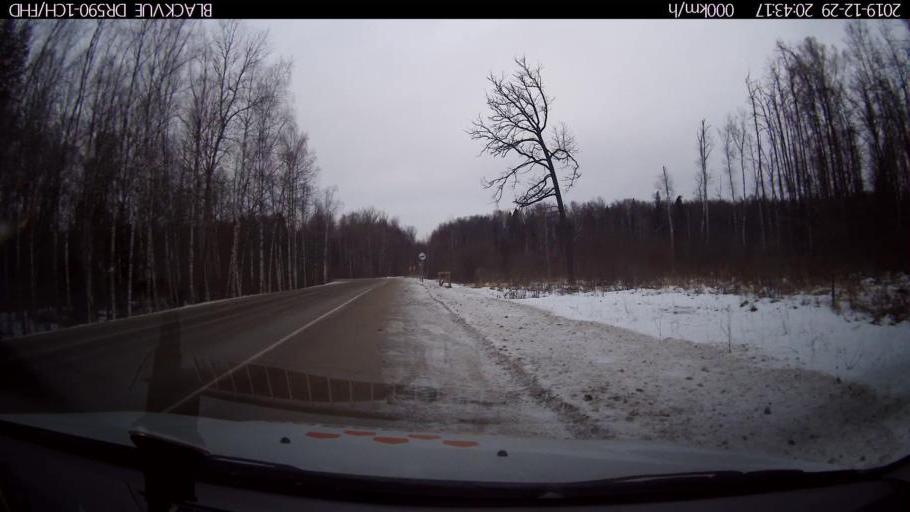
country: RU
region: Nizjnij Novgorod
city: Afonino
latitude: 56.1909
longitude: 44.0287
